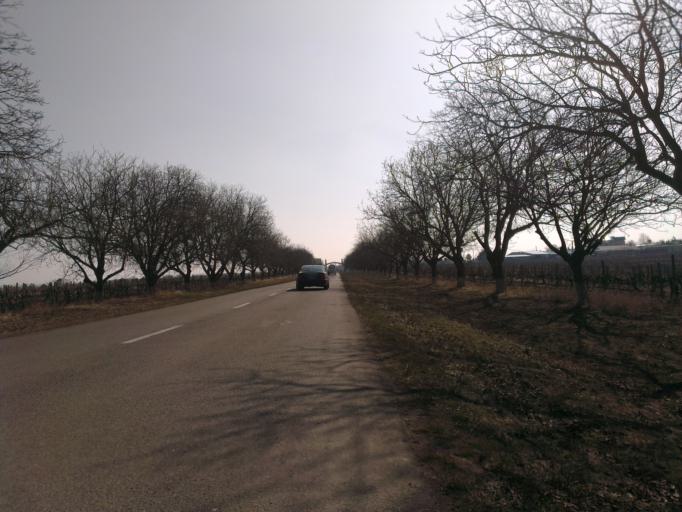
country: MD
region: Chisinau
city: Cricova
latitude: 47.1197
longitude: 28.8596
